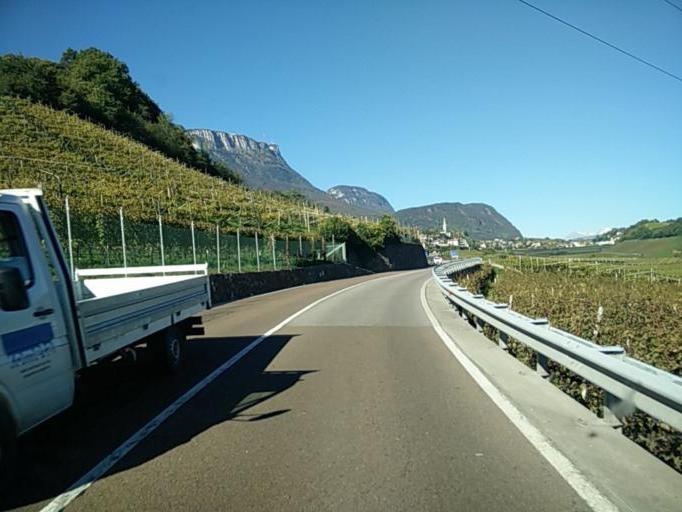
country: IT
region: Trentino-Alto Adige
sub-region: Bolzano
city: Caldaro sulla Strada del Vino
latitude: 46.4007
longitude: 11.2501
